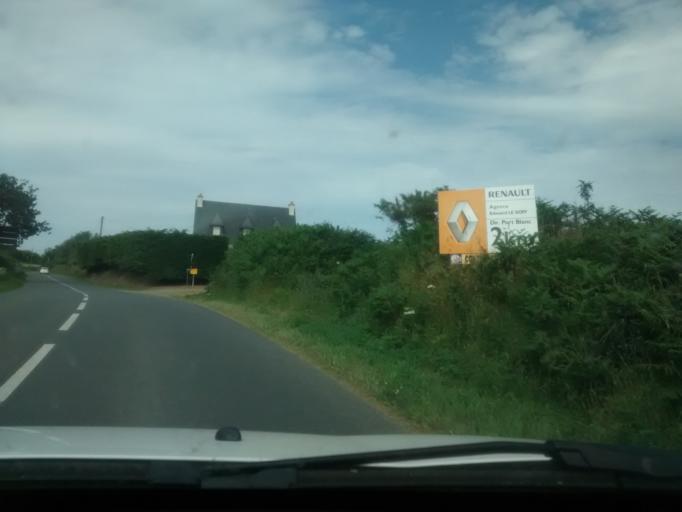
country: FR
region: Brittany
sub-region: Departement des Cotes-d'Armor
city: Penvenan
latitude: 48.7986
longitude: -3.3119
